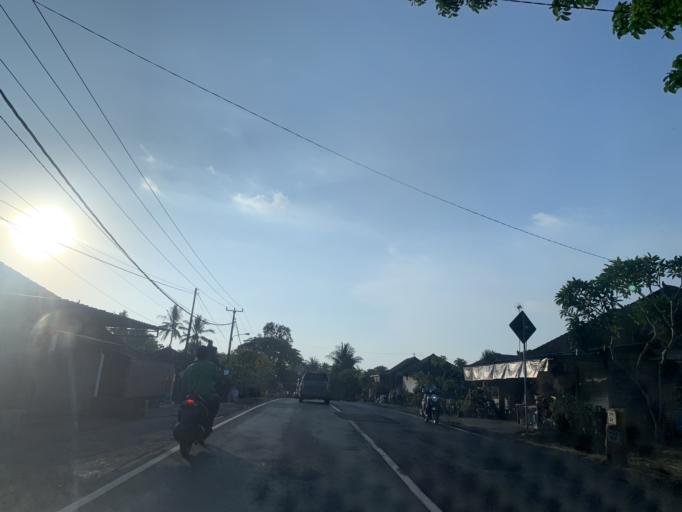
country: ID
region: Bali
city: Banjar Delodrurung
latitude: -8.4928
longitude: 114.9611
